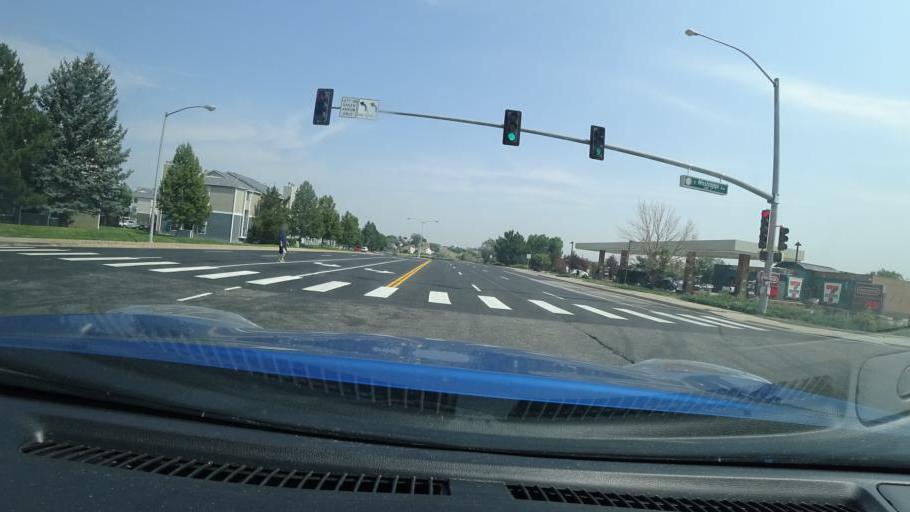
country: US
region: Colorado
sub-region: Adams County
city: Aurora
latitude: 39.6966
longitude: -104.7722
